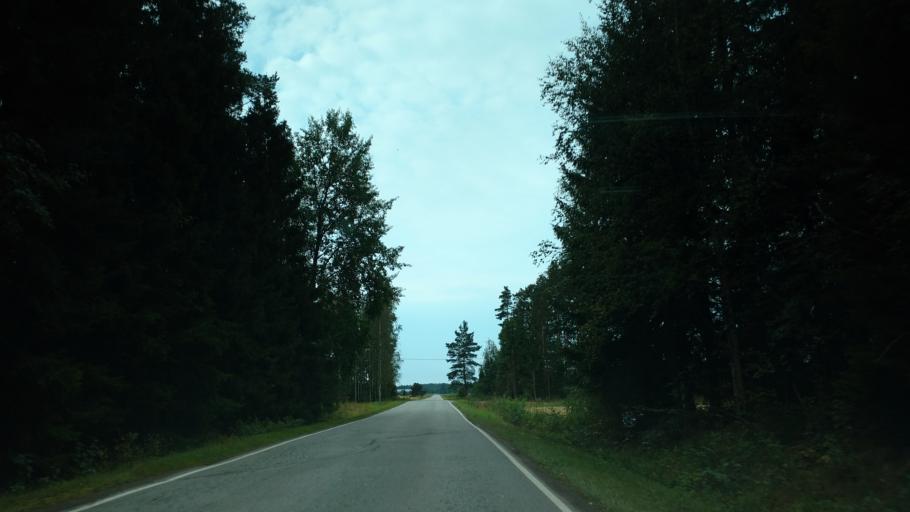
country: FI
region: Varsinais-Suomi
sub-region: Loimaa
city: Koski Tl
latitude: 60.7257
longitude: 23.1813
